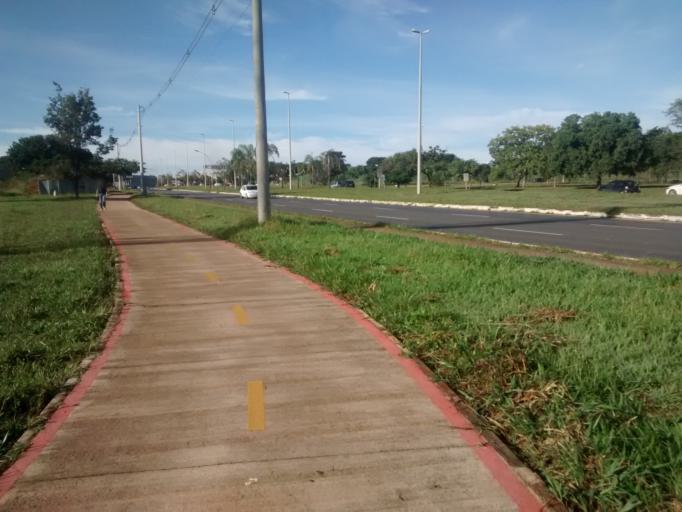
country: BR
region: Federal District
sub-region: Brasilia
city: Brasilia
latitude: -15.7653
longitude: -47.8733
